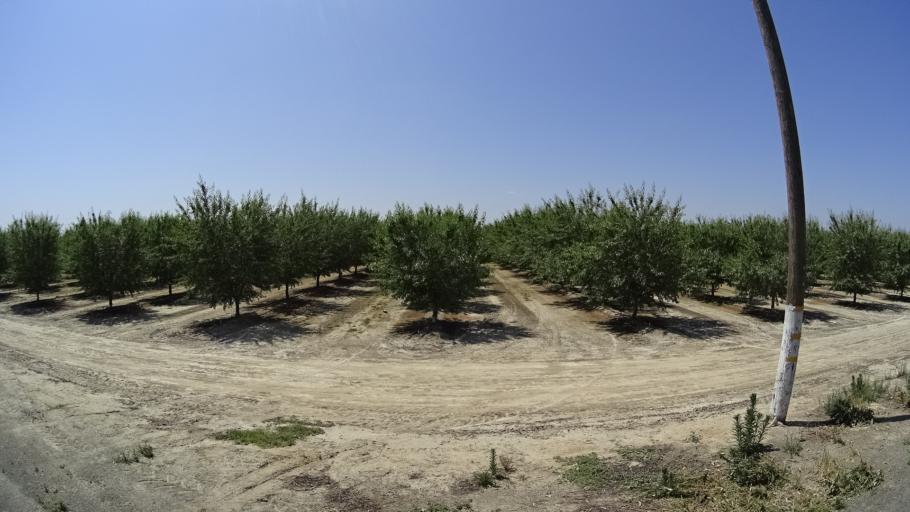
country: US
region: California
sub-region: Kings County
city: Home Garden
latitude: 36.2840
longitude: -119.5943
